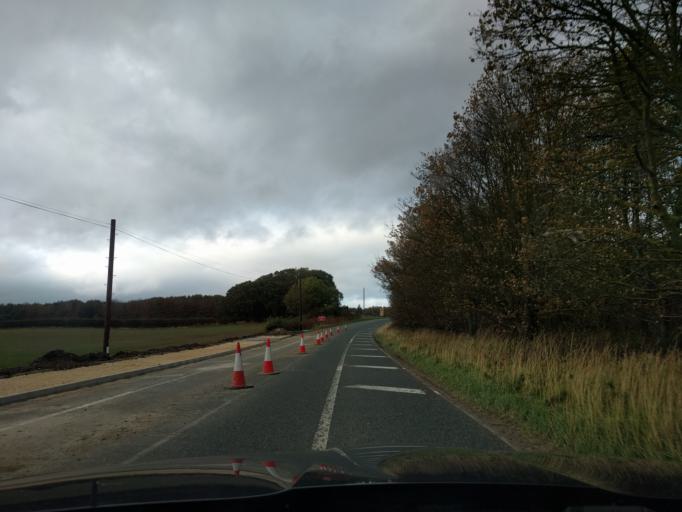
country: GB
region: England
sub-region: Northumberland
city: Cramlington
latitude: 55.0823
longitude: -1.6274
